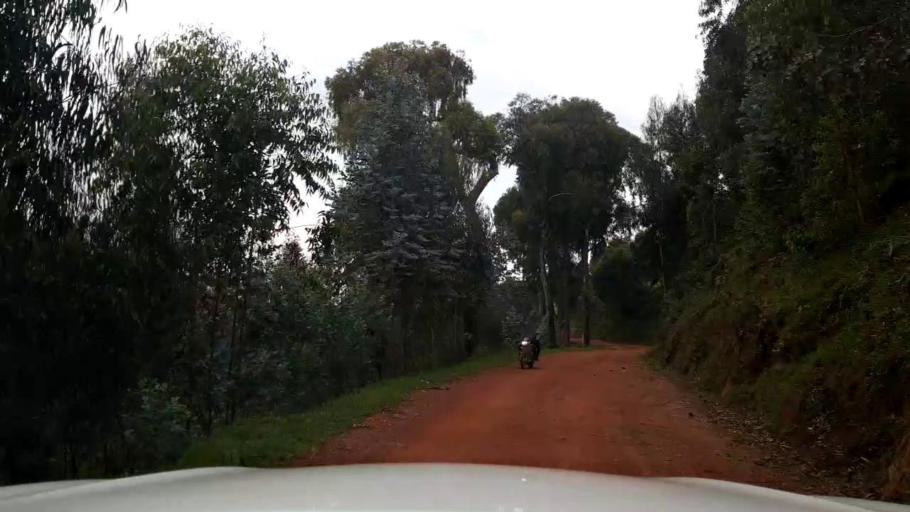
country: RW
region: Northern Province
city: Byumba
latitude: -1.5240
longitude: 29.9529
